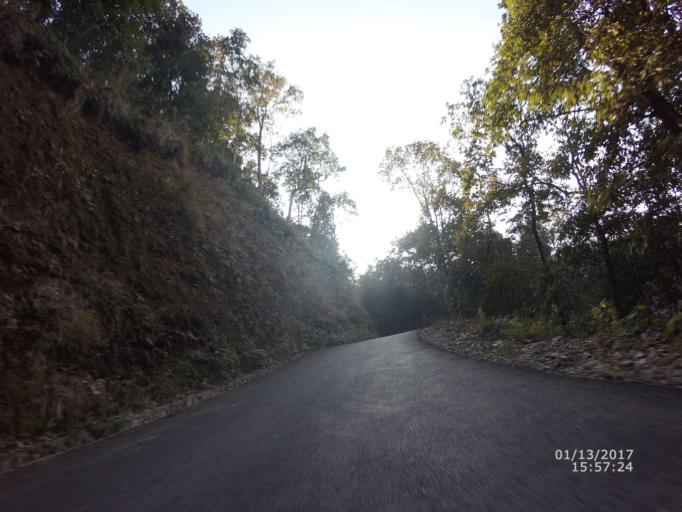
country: NP
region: Western Region
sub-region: Gandaki Zone
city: Pokhara
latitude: 28.1607
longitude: 84.0016
